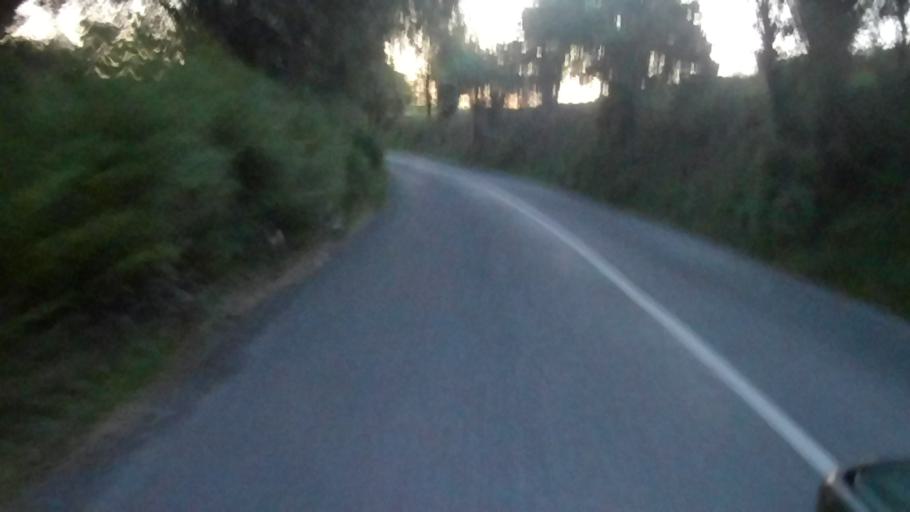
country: IE
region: Munster
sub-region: County Cork
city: Carrigtwohill
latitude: 51.9386
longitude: -8.3233
